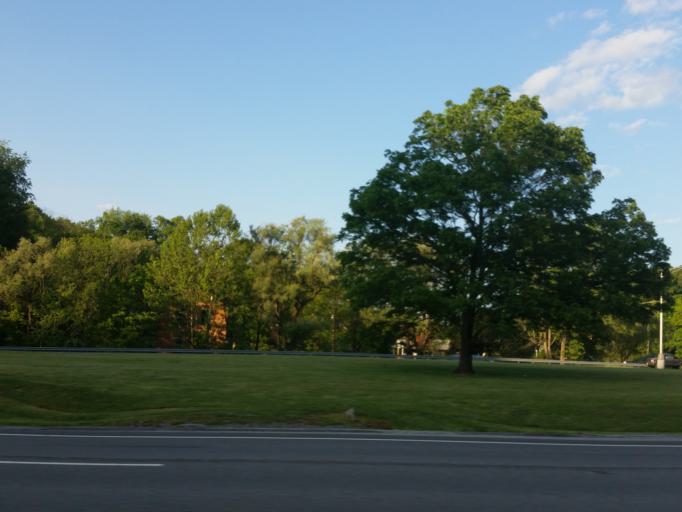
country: US
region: Virginia
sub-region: Washington County
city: Abingdon
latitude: 36.7474
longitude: -82.0532
